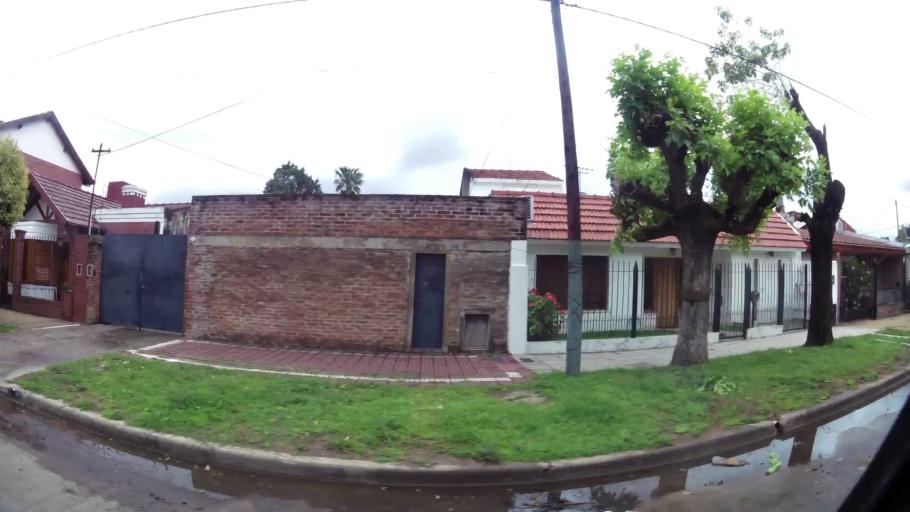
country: AR
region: Buenos Aires
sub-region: Partido de Lomas de Zamora
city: Lomas de Zamora
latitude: -34.7480
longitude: -58.3819
